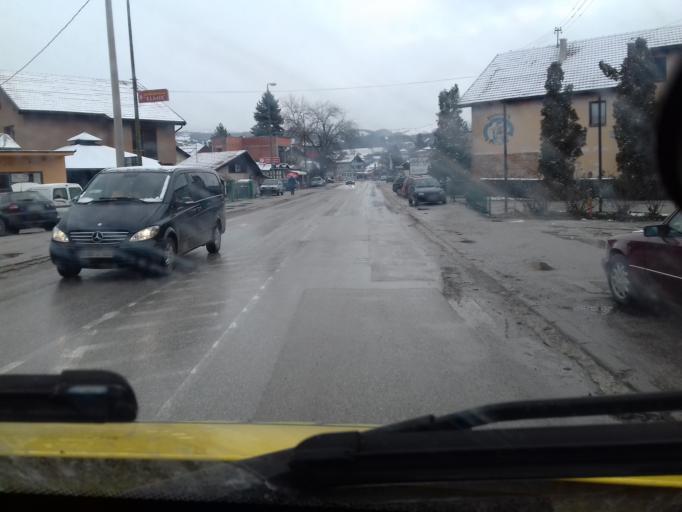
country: BA
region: Federation of Bosnia and Herzegovina
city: Kakanj
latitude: 44.1219
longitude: 18.1078
